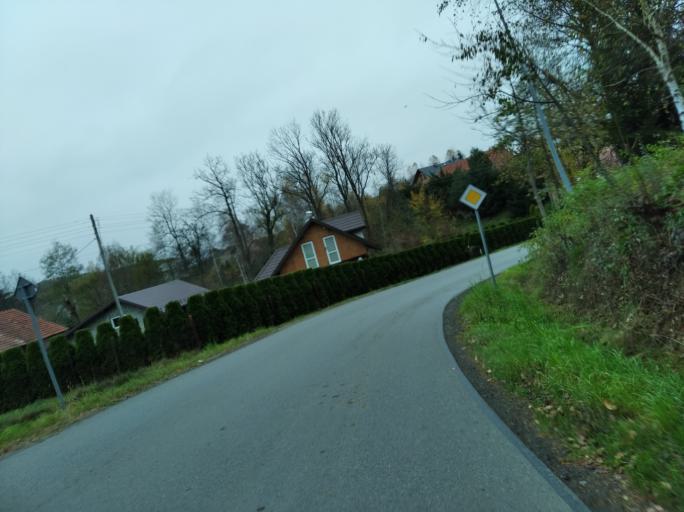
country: PL
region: Subcarpathian Voivodeship
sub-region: Powiat krosnienski
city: Jedlicze
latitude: 49.7323
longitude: 21.6504
